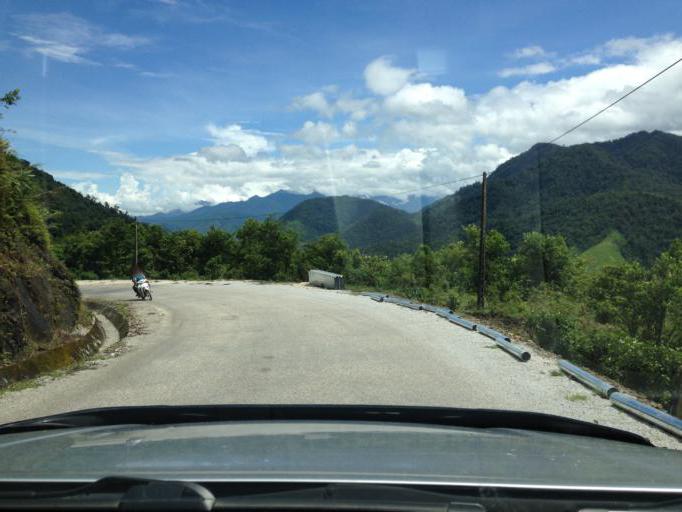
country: VN
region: Lai Chau
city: Than Uyen
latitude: 22.0457
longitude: 103.9678
